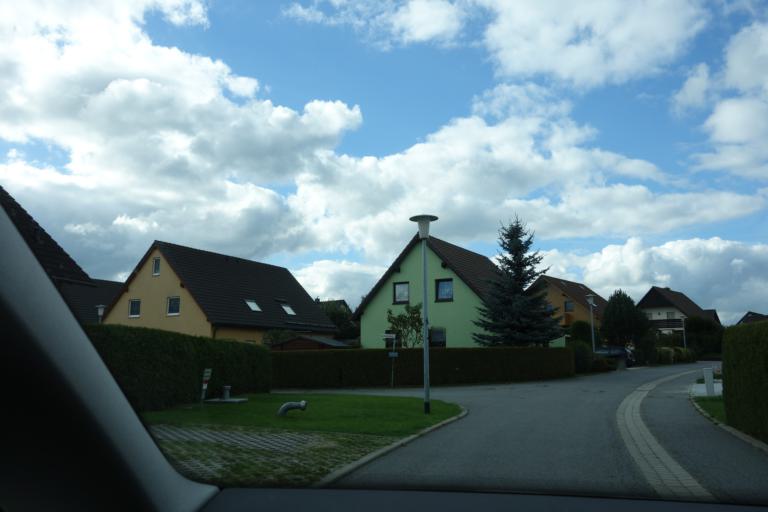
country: DE
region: Saxony
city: Grossolbersdorf
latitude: 50.7236
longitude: 13.0883
